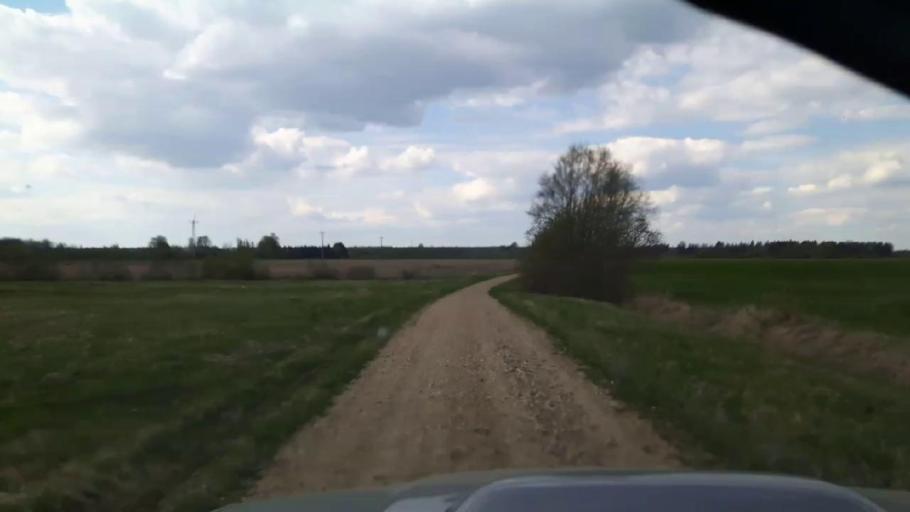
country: EE
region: Paernumaa
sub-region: Sindi linn
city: Sindi
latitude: 58.4336
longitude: 24.7504
